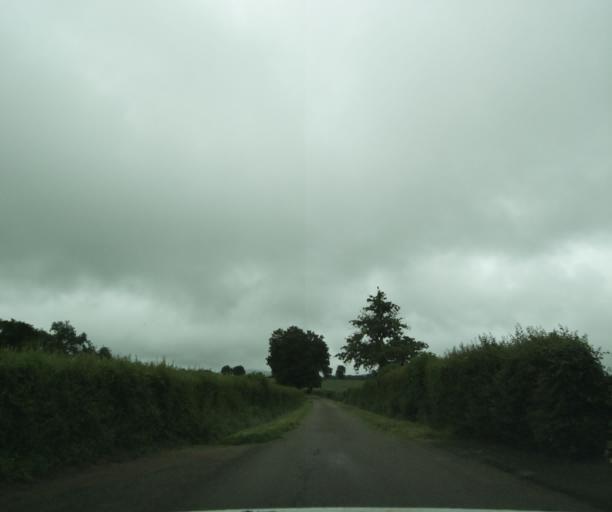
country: FR
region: Bourgogne
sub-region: Departement de Saone-et-Loire
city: Charolles
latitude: 46.4310
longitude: 4.3239
